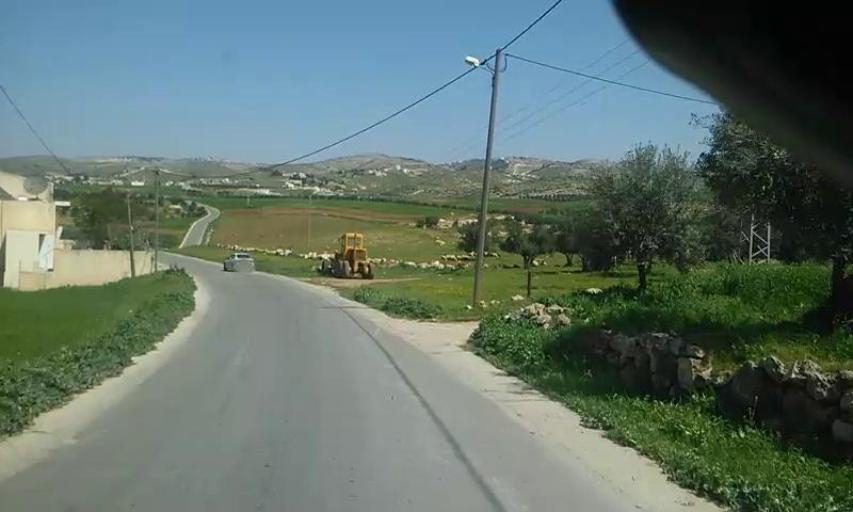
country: PS
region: West Bank
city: Dayr al `Asal al Fawqa
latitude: 31.4676
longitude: 34.9421
